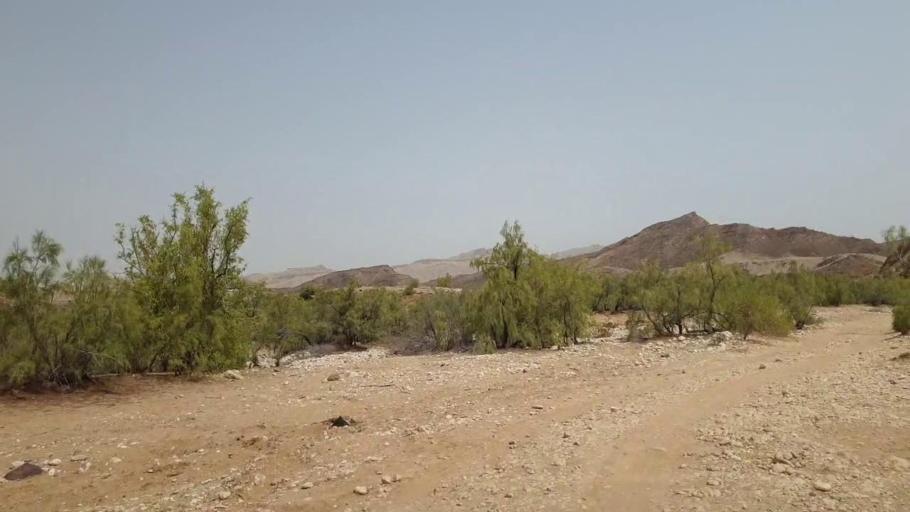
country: PK
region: Sindh
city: Sann
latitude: 25.8836
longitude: 67.9218
